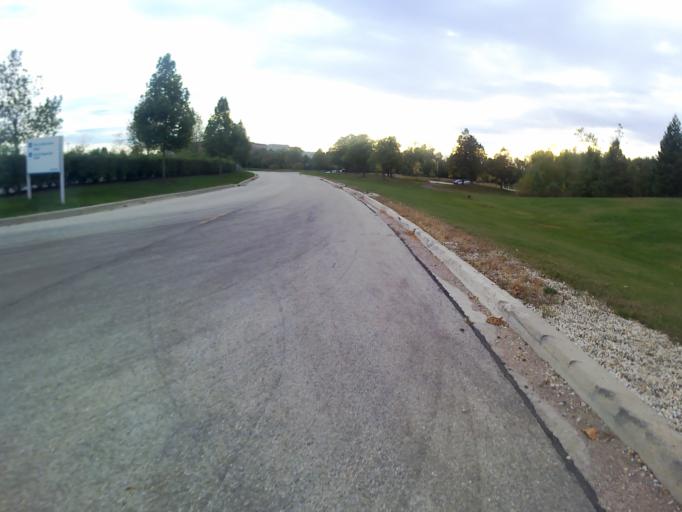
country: US
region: Illinois
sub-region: DuPage County
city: Lisle
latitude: 41.8134
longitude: -88.1103
